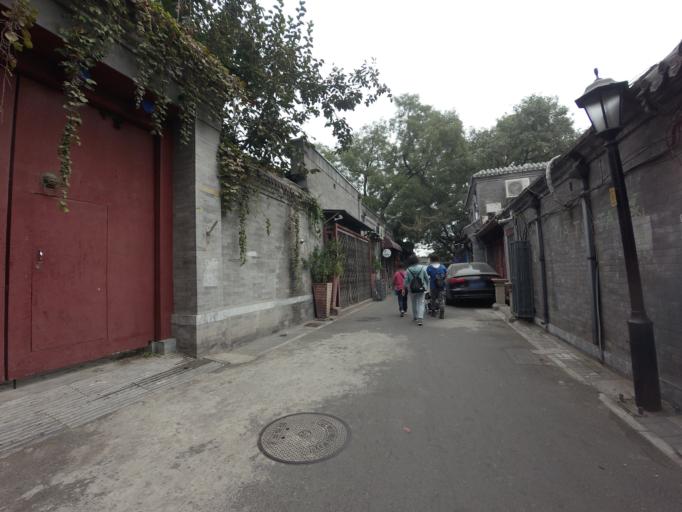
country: CN
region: Beijing
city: Jingshan
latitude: 39.9389
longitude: 116.3856
